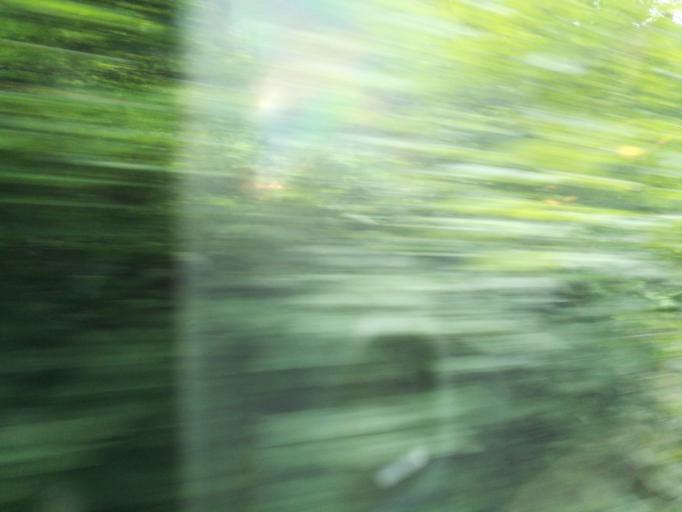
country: RO
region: Brasov
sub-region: Oras Predeal
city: Predeal
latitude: 45.5183
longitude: 25.5944
